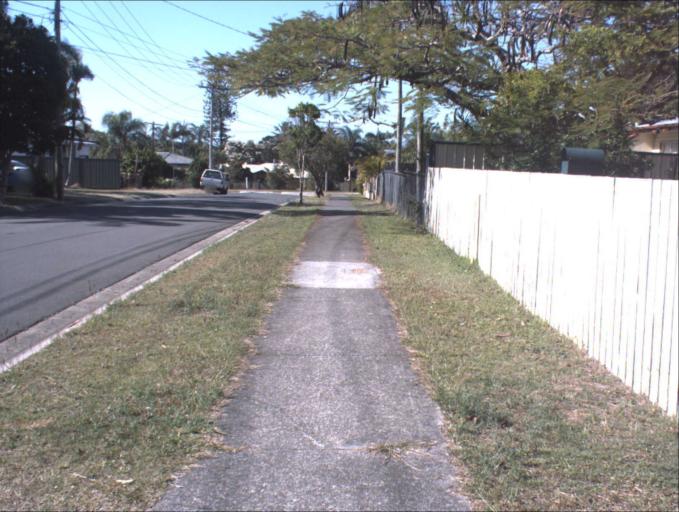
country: AU
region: Queensland
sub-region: Logan
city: Logan City
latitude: -27.6574
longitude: 153.1092
